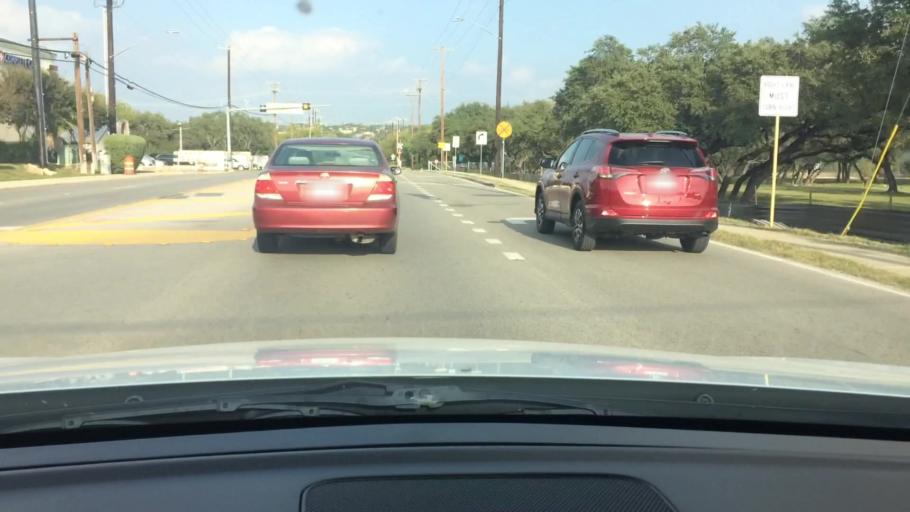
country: US
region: Texas
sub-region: Bexar County
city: Shavano Park
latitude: 29.5676
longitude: -98.5798
